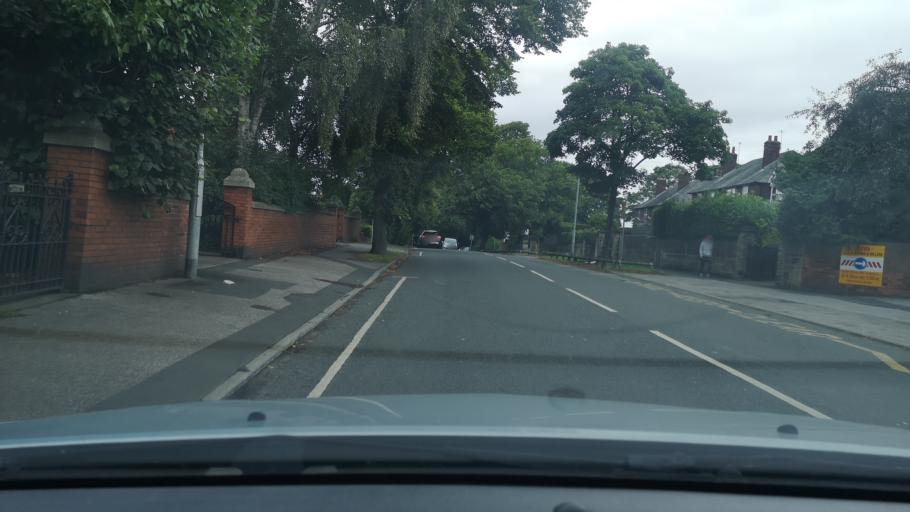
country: GB
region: England
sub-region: City and Borough of Wakefield
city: Wakefield
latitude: 53.6794
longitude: -1.5287
